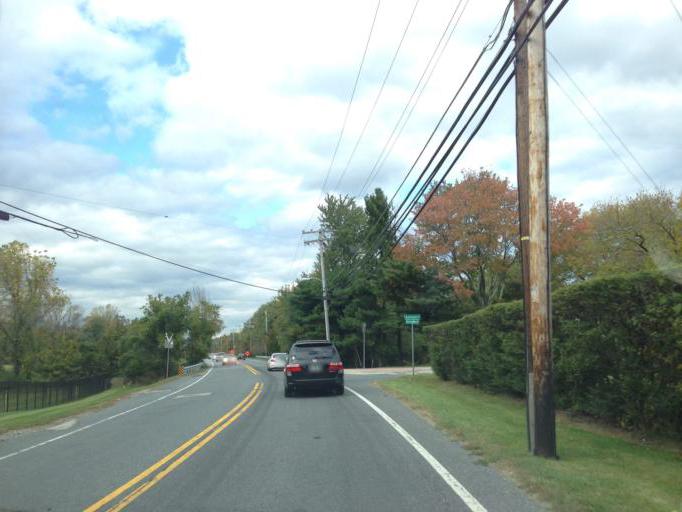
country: US
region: Maryland
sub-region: Baltimore County
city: Pikesville
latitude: 39.3828
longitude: -76.7177
